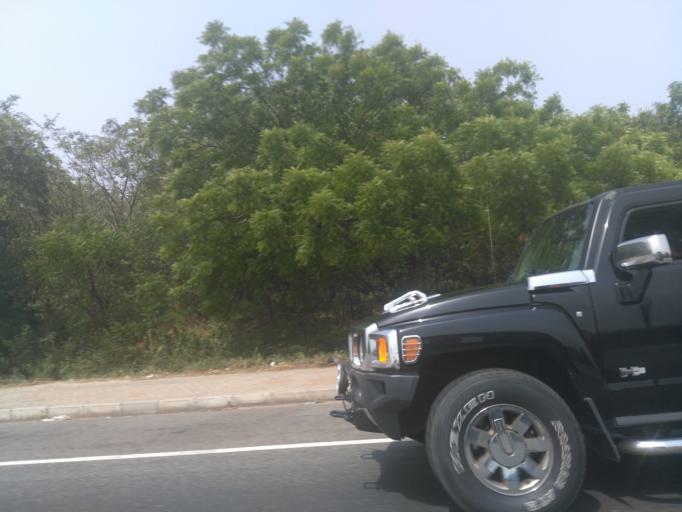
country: GH
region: Greater Accra
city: Dome
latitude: 5.6161
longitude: -0.2064
